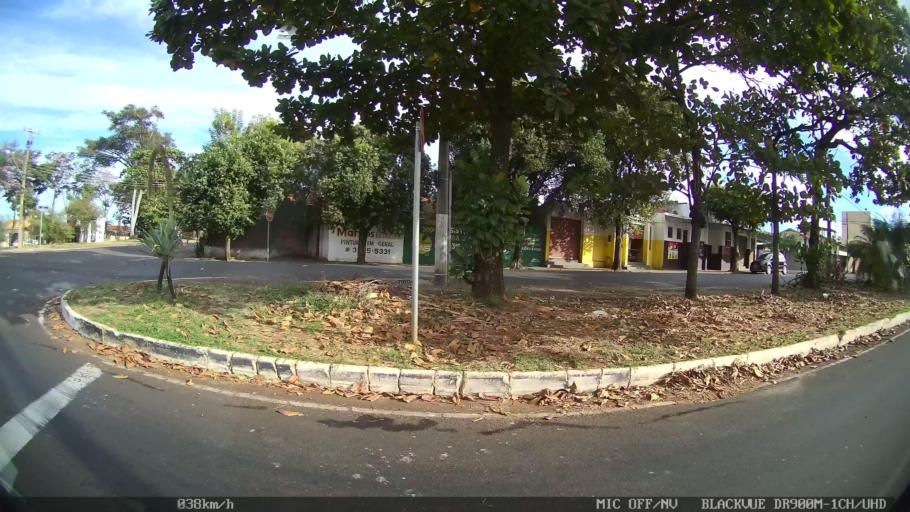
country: BR
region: Sao Paulo
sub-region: Catanduva
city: Catanduva
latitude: -21.1163
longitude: -48.9641
